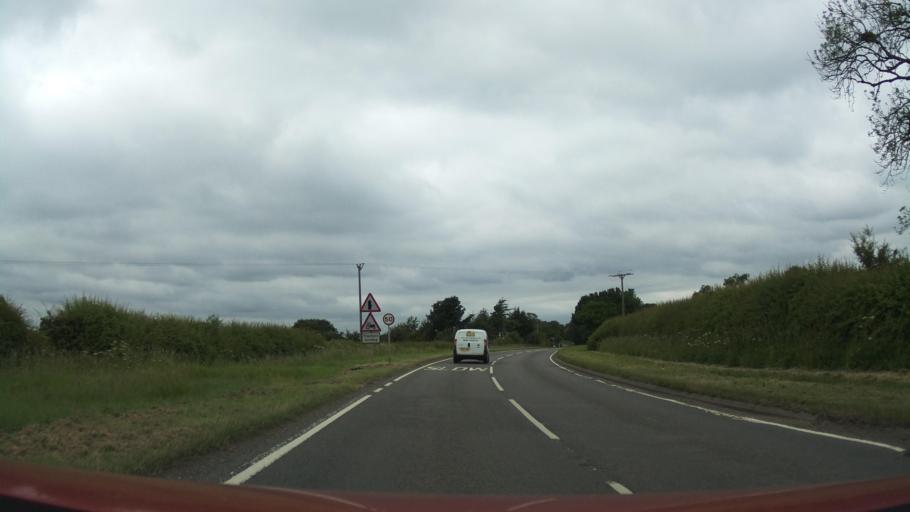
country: GB
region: England
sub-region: Leicestershire
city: Grimston
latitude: 52.7921
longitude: -1.0291
